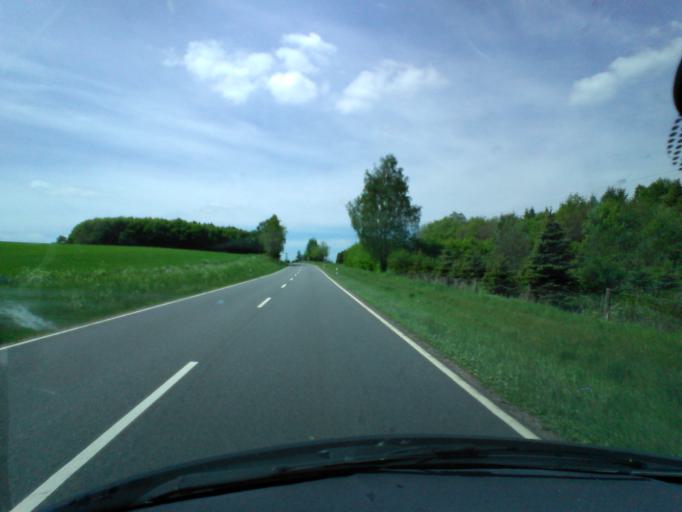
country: DE
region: Rheinland-Pfalz
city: Arzfeld
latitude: 50.0859
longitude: 6.2583
